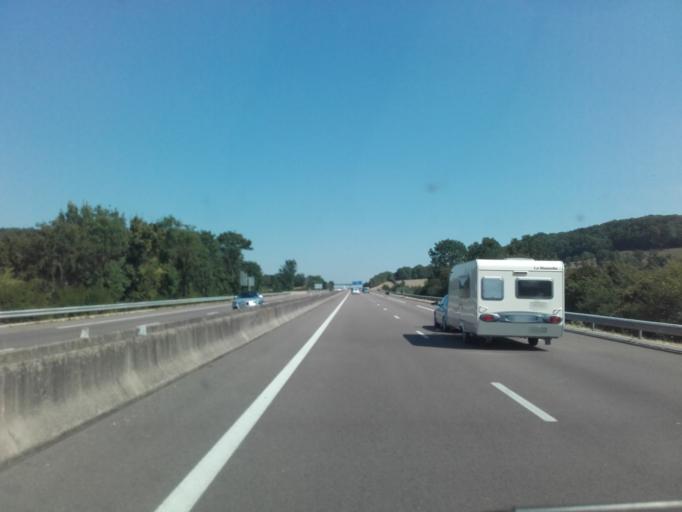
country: FR
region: Bourgogne
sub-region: Departement de la Cote-d'Or
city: Pouilly-en-Auxois
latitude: 47.2554
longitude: 4.5391
